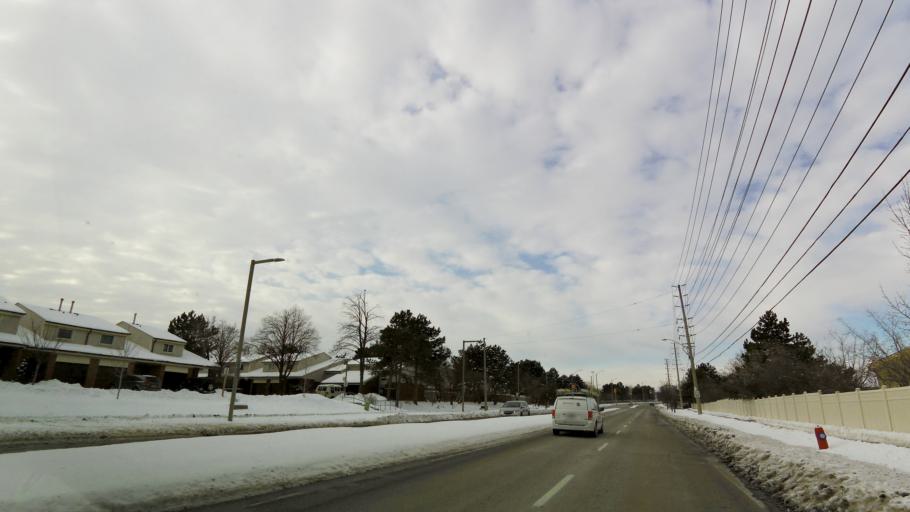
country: CA
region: Ontario
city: Mississauga
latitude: 43.5467
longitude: -79.6975
